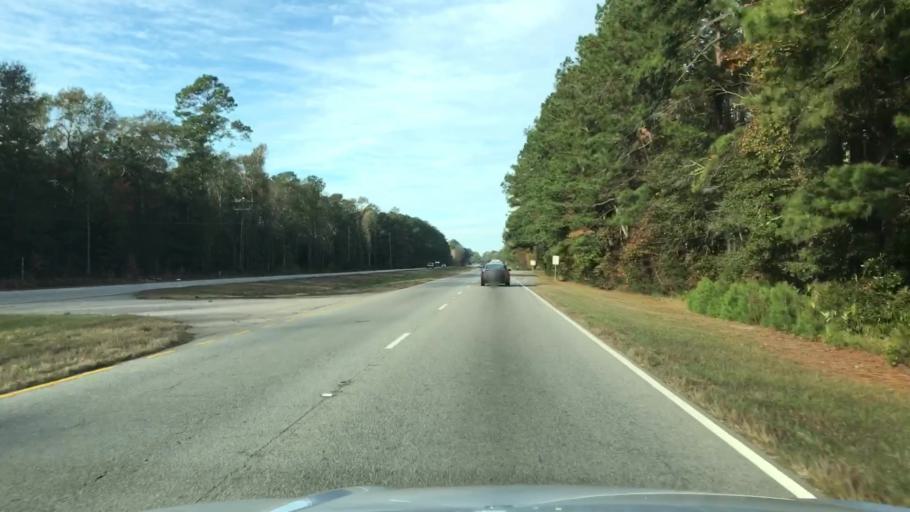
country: US
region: South Carolina
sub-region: Charleston County
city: Ravenel
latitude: 32.7816
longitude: -80.1913
